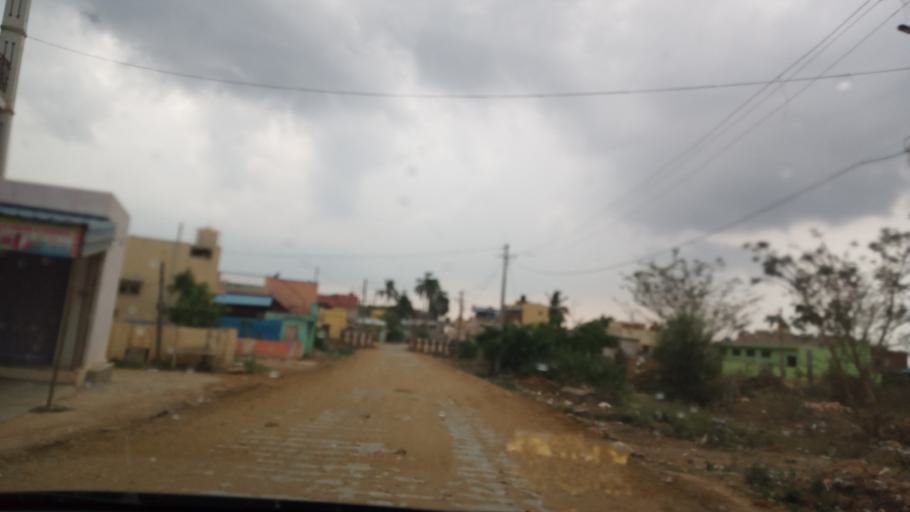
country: IN
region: Karnataka
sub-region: Kolar
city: Mulbagal
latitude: 13.1459
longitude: 78.3692
